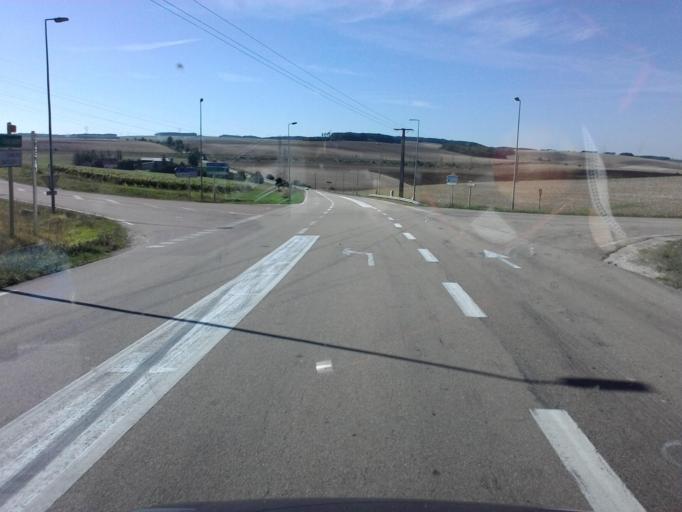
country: FR
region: Bourgogne
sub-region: Departement de l'Yonne
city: Tonnerre
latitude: 47.8435
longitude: 3.9564
